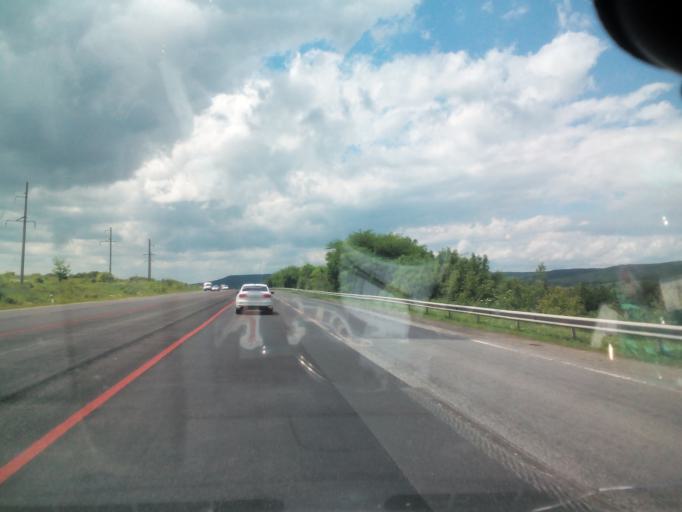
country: RU
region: Stavropol'skiy
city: Tatarka
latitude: 44.9516
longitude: 41.9523
